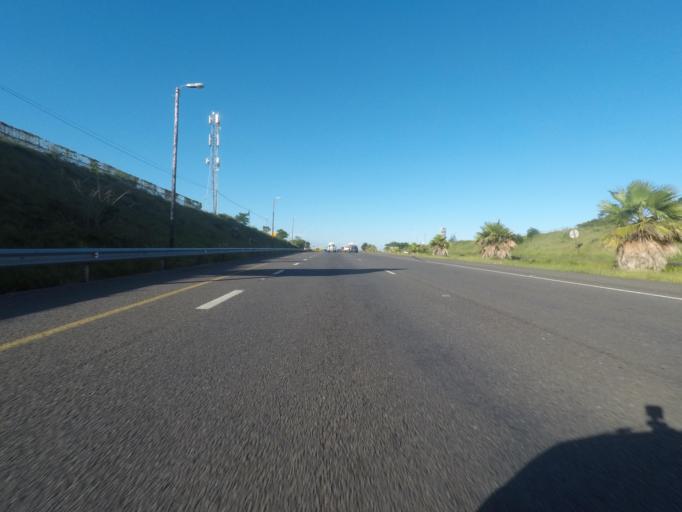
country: ZA
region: Eastern Cape
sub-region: Buffalo City Metropolitan Municipality
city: East London
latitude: -33.0398
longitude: 27.8313
